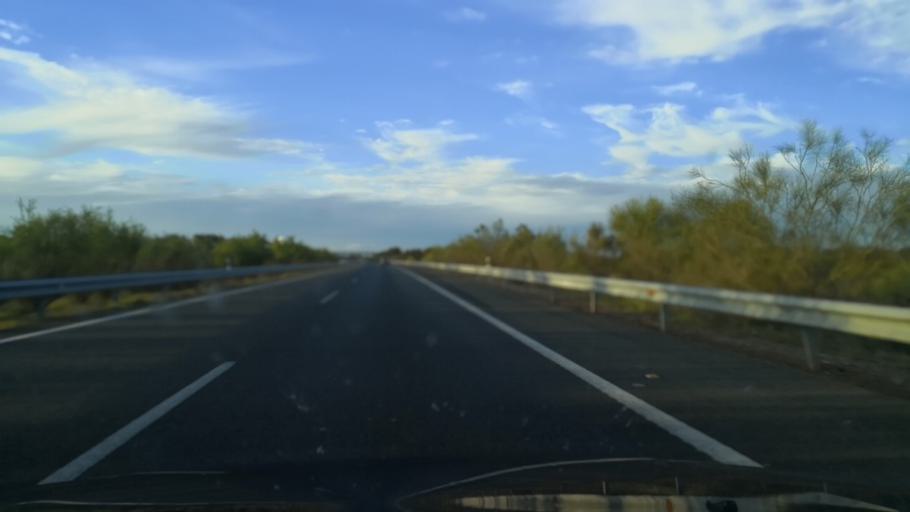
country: ES
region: Extremadura
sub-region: Provincia de Badajoz
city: Aljucen
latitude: 39.0060
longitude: -6.3308
